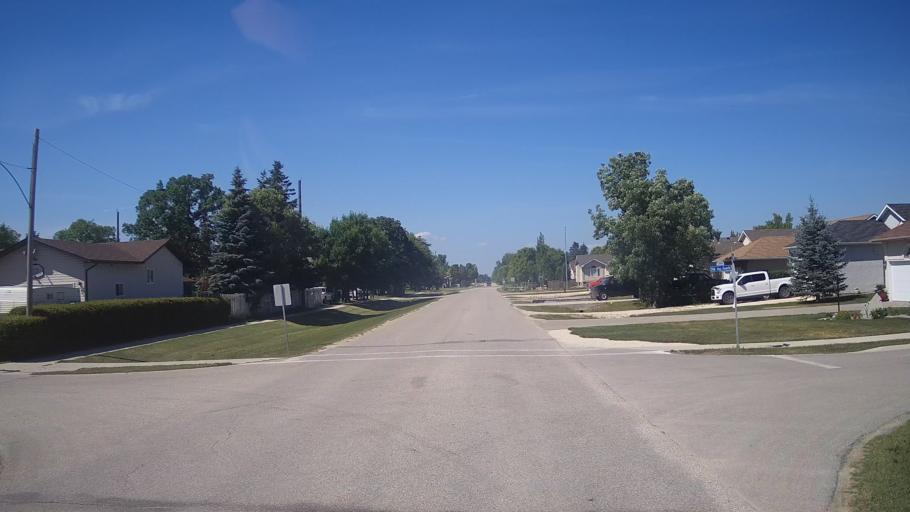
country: CA
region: Manitoba
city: Stonewall
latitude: 50.1278
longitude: -97.3333
